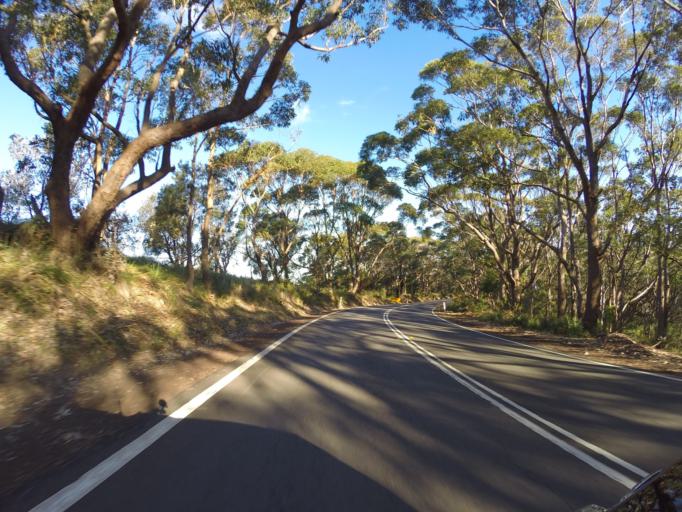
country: AU
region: New South Wales
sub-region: Wollongong
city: Helensburgh
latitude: -34.2202
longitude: 150.9998
